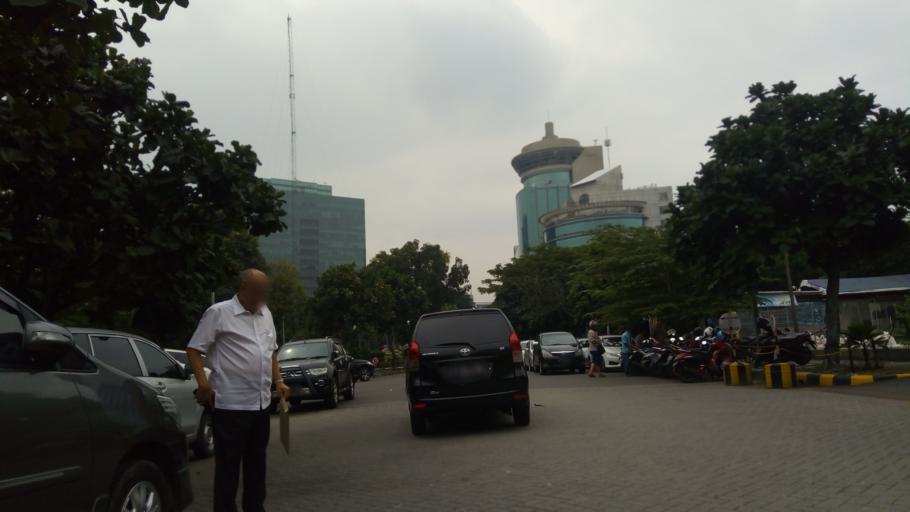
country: ID
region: Jakarta Raya
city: Jakarta
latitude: -6.1563
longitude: 106.8424
